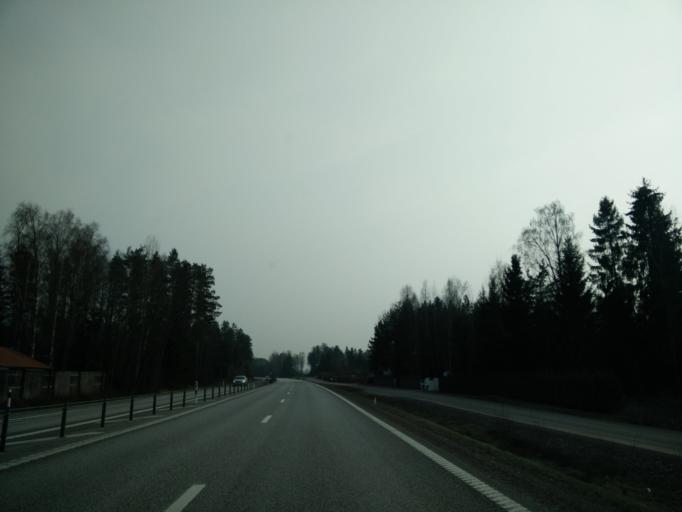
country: SE
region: Vaermland
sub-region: Forshaga Kommun
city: Forshaga
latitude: 59.4801
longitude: 13.4113
